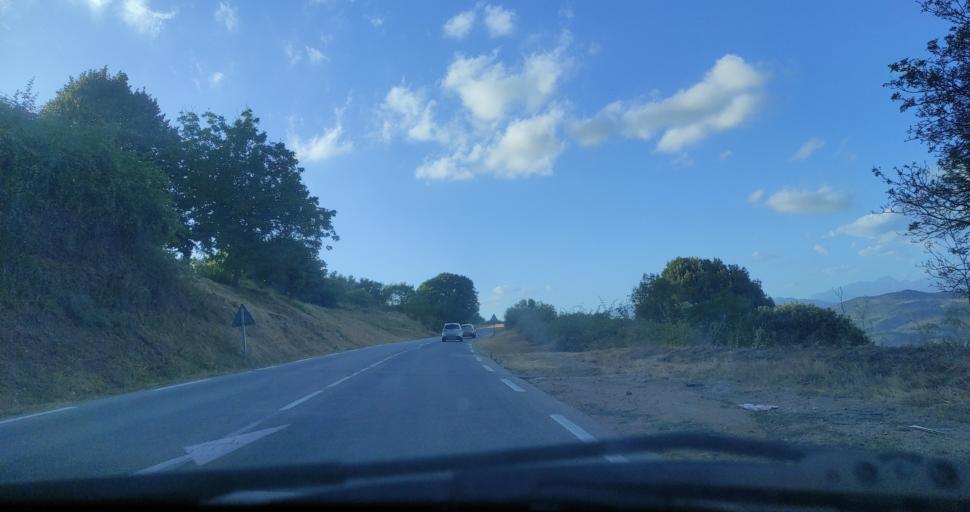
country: FR
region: Corsica
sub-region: Departement de la Corse-du-Sud
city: Appietto
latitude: 42.0317
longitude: 8.7647
